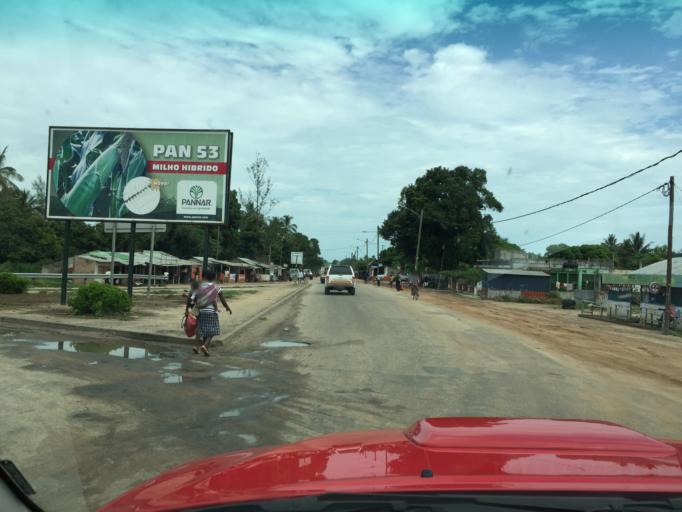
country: MZ
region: Zambezia
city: Quelimane
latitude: -17.5948
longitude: 36.8150
